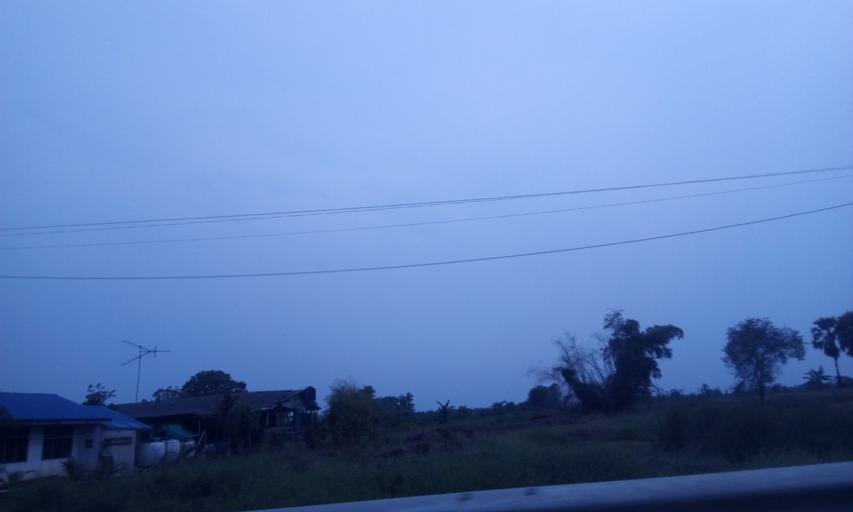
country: TH
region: Chachoengsao
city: Plaeng Yao
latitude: 13.5873
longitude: 101.2126
